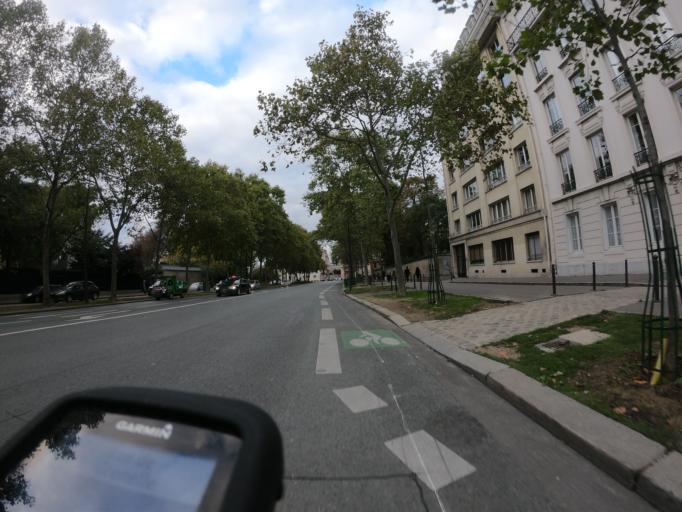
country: FR
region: Ile-de-France
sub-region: Paris
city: Paris
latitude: 48.8564
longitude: 2.3152
